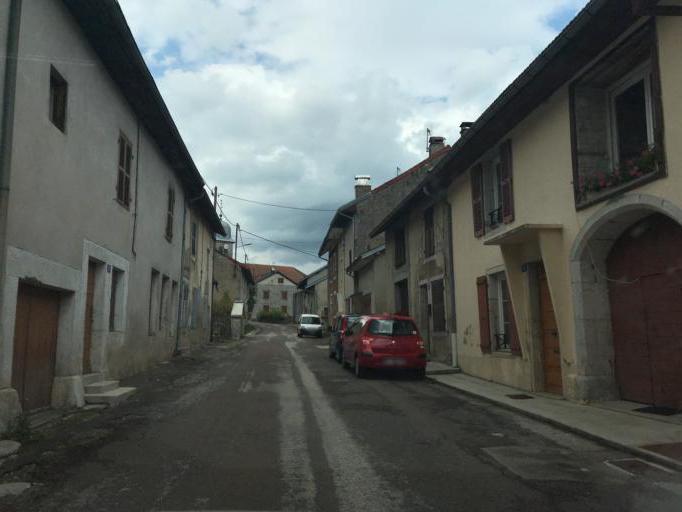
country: FR
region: Franche-Comte
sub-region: Departement du Jura
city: Valfin-les-Saint-Claude
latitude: 46.4374
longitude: 5.8547
